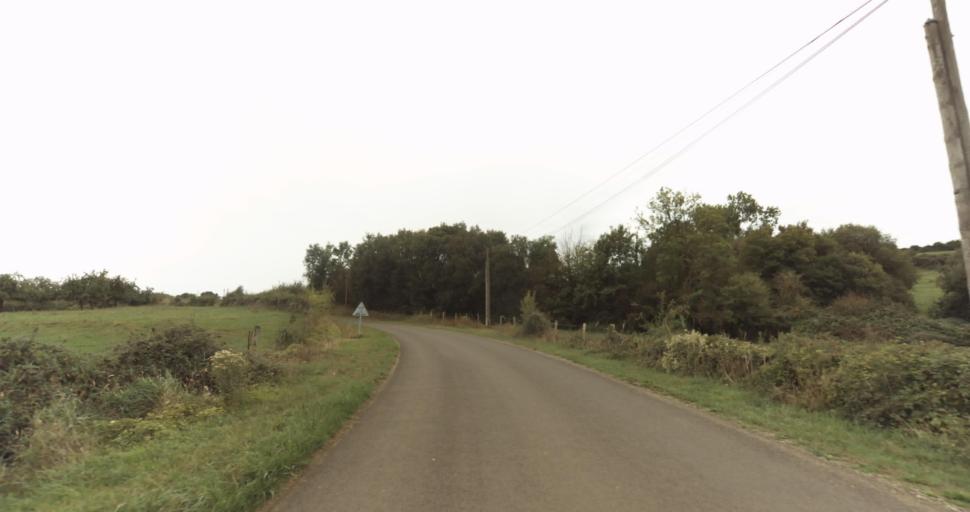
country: FR
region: Lower Normandy
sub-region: Departement de l'Orne
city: Gace
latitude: 48.7635
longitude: 0.3294
